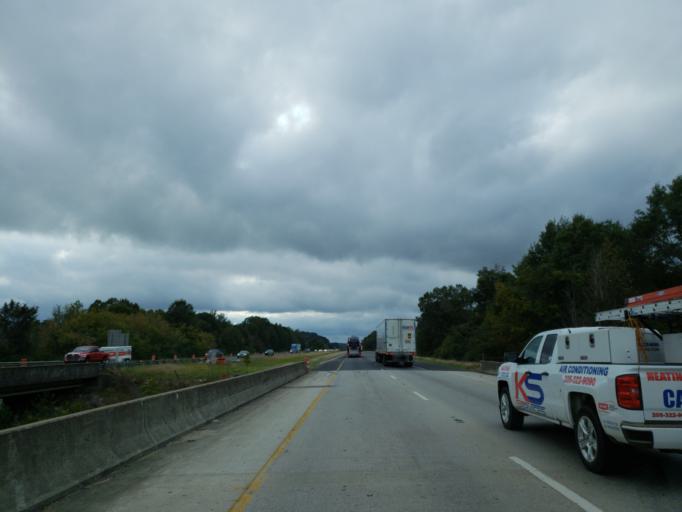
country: US
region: Alabama
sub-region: Jefferson County
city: Bessemer
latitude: 33.3361
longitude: -86.9398
